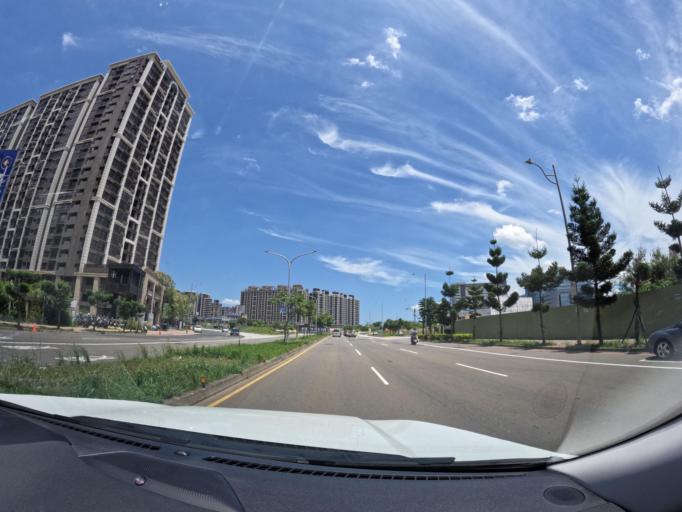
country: TW
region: Taipei
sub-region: Taipei
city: Banqiao
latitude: 25.0473
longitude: 121.3857
